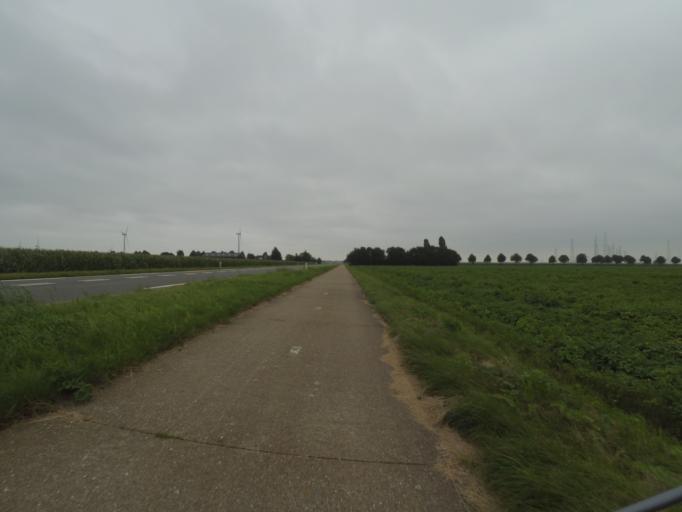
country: NL
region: Flevoland
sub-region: Gemeente Zeewolde
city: Zeewolde
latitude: 52.3723
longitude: 5.4588
